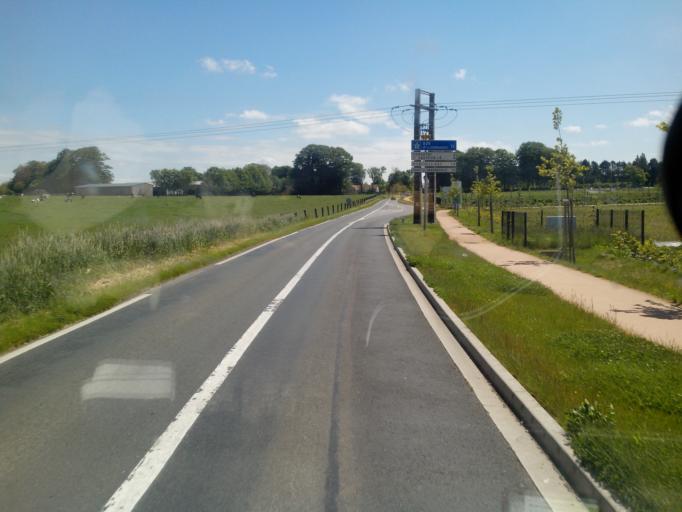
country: FR
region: Haute-Normandie
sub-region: Departement de la Seine-Maritime
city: Turretot
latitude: 49.6370
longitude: 0.2697
